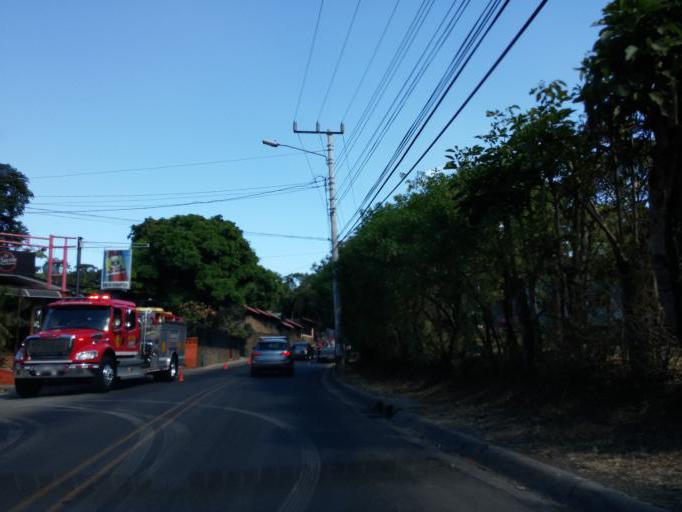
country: CR
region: Heredia
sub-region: Canton de Belen
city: San Antonio
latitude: 9.9861
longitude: -84.1952
